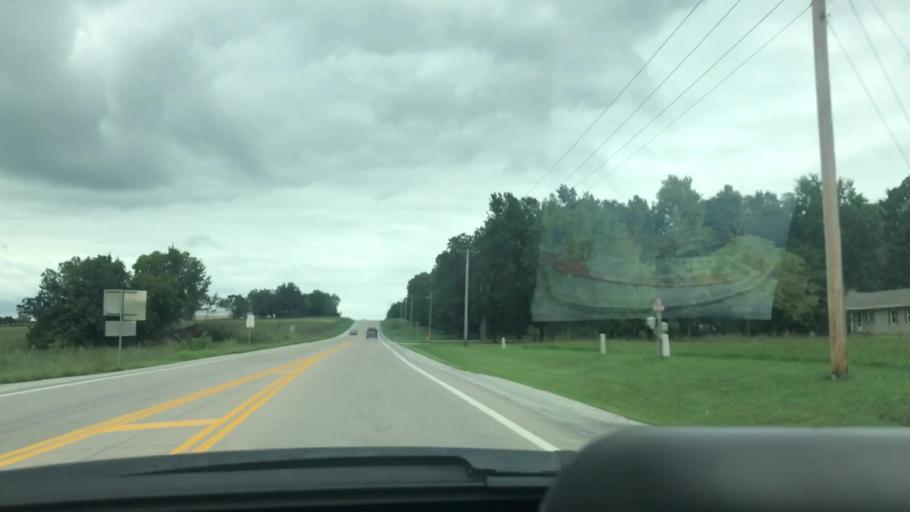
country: US
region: Missouri
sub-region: Dallas County
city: Buffalo
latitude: 37.6695
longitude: -93.1033
